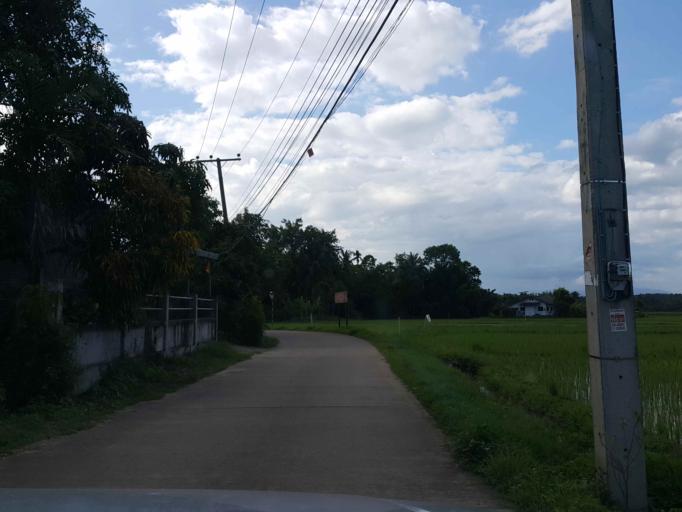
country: TH
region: Chiang Mai
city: Mae Taeng
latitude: 18.9684
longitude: 98.9170
